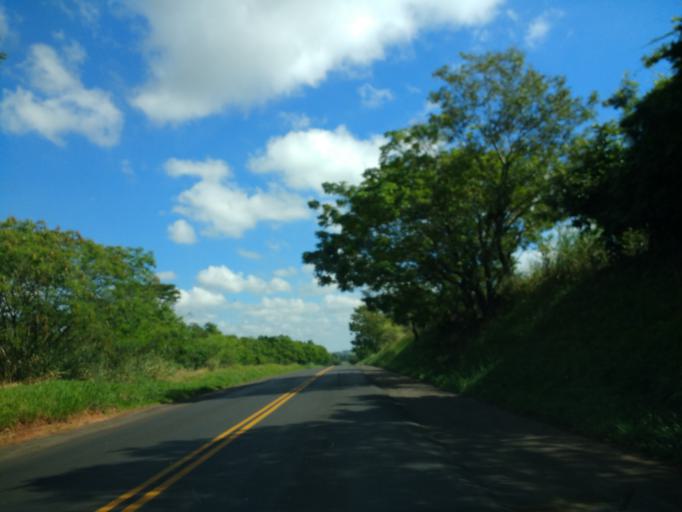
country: BR
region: Parana
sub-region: Umuarama
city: Umuarama
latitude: -23.8621
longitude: -53.3851
